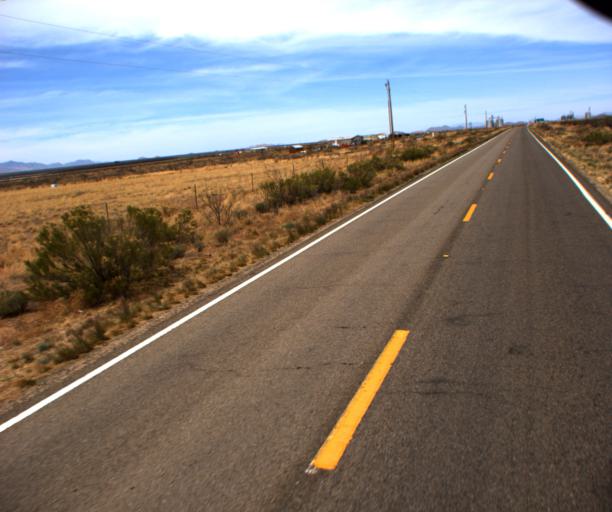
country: US
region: Arizona
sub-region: Cochise County
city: Bisbee
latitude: 31.7413
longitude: -109.6880
